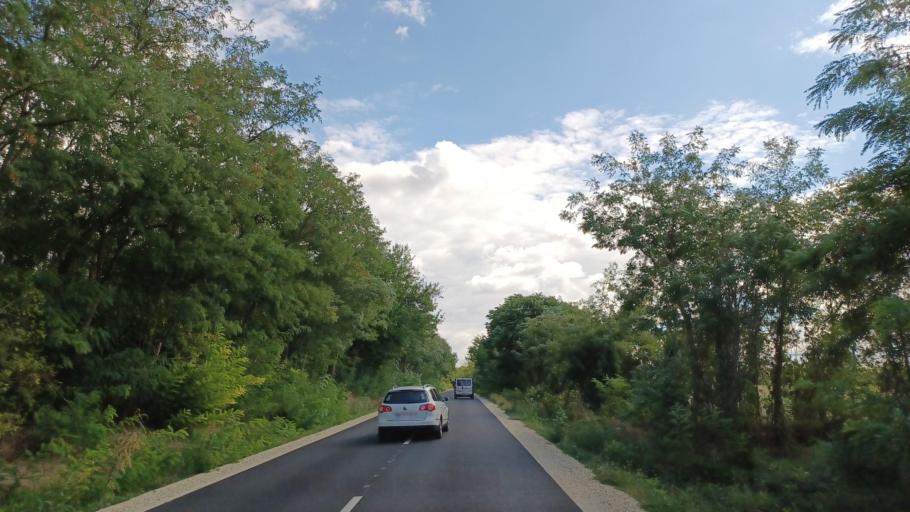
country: HU
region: Tolna
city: Nagydorog
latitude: 46.6024
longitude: 18.6981
